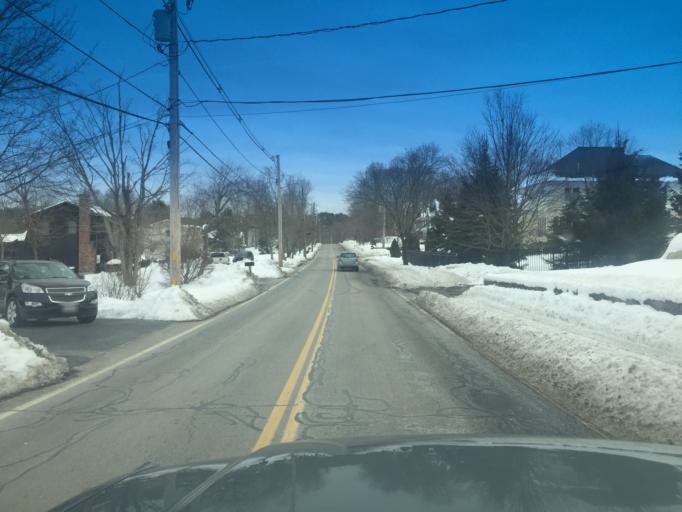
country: US
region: Massachusetts
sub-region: Norfolk County
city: Norfolk
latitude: 42.1028
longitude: -71.2805
